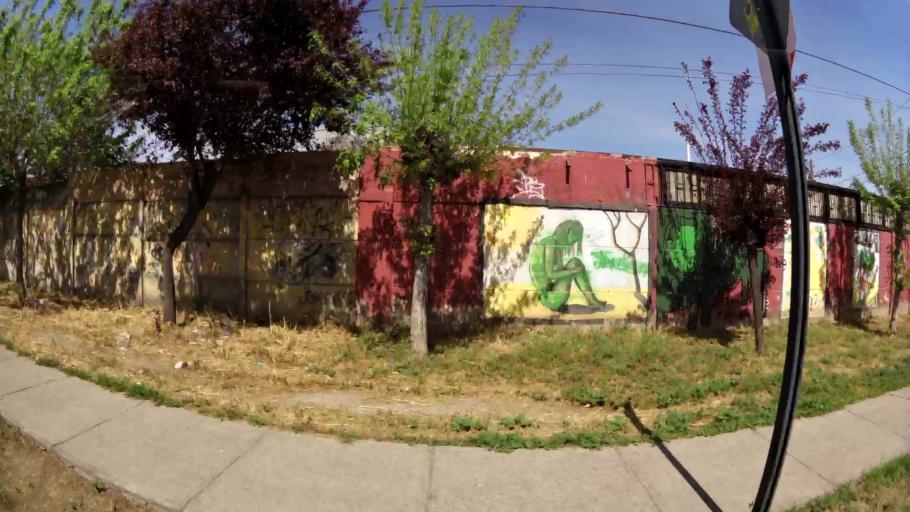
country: CL
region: Santiago Metropolitan
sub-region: Provincia de Cordillera
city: Puente Alto
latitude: -33.5704
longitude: -70.5744
